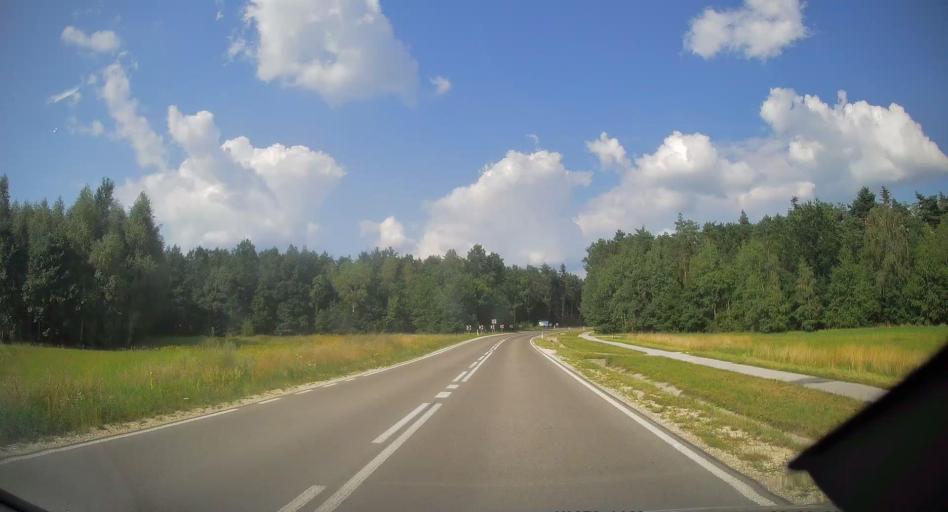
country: PL
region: Swietokrzyskie
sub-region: Powiat kielecki
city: Lopuszno
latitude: 51.0044
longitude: 20.2734
